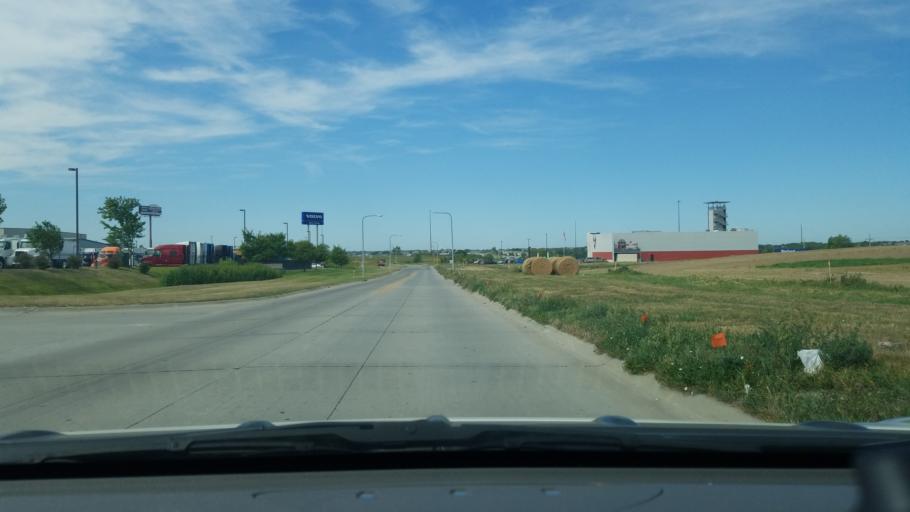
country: US
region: Nebraska
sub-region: Sarpy County
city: Chalco
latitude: 41.1456
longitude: -96.1523
